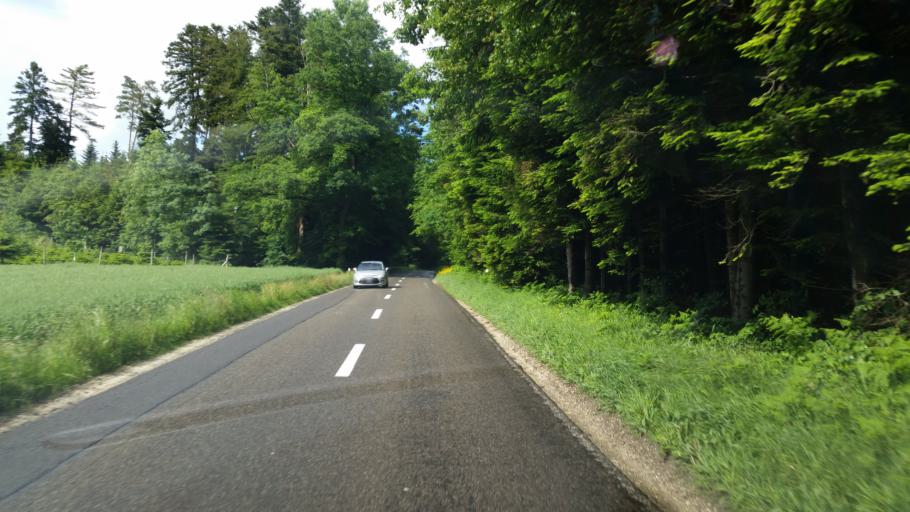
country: CH
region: Aargau
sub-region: Bezirk Muri
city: Waltenschwil
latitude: 47.3356
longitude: 8.3202
